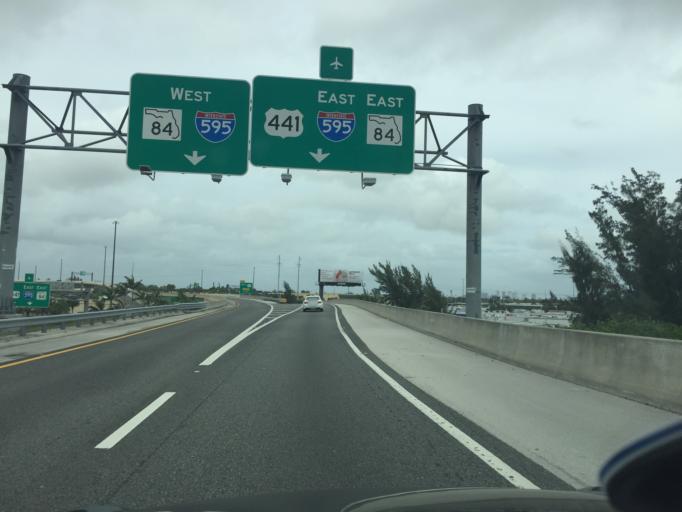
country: US
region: Florida
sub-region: Broward County
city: Broadview Park
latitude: 26.0852
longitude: -80.2213
